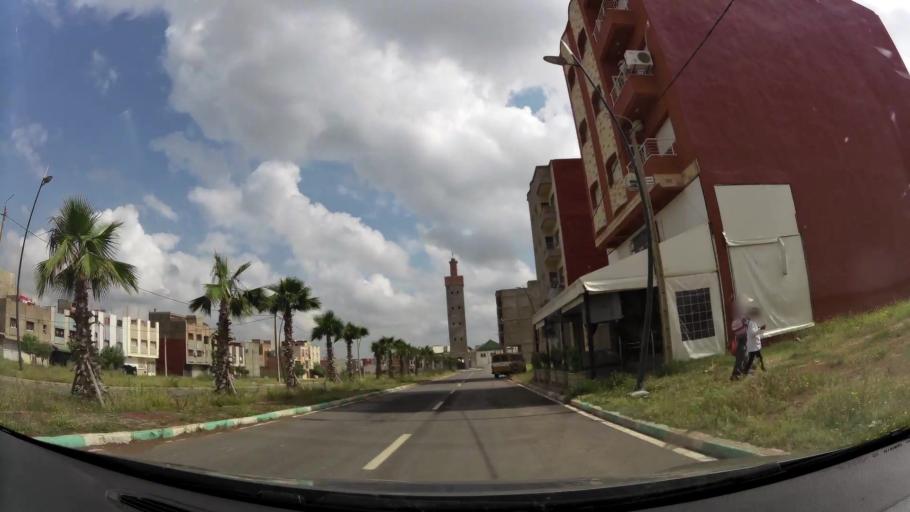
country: MA
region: Rabat-Sale-Zemmour-Zaer
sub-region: Khemisset
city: Tiflet
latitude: 33.8973
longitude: -6.3385
